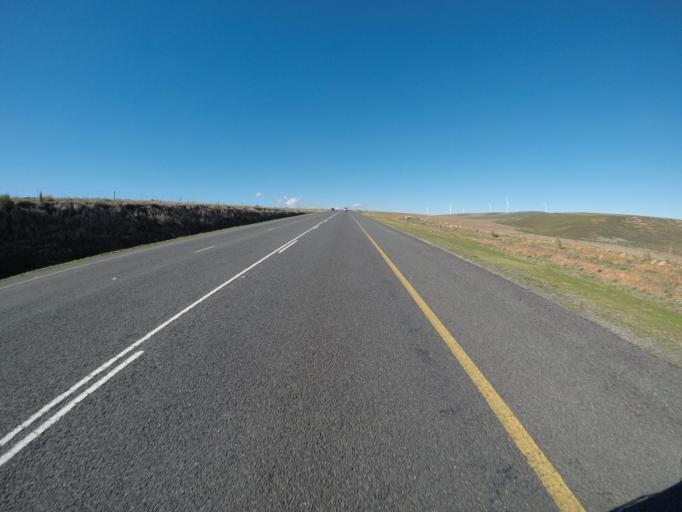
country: ZA
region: Western Cape
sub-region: Overberg District Municipality
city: Caledon
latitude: -34.2114
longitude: 19.3492
